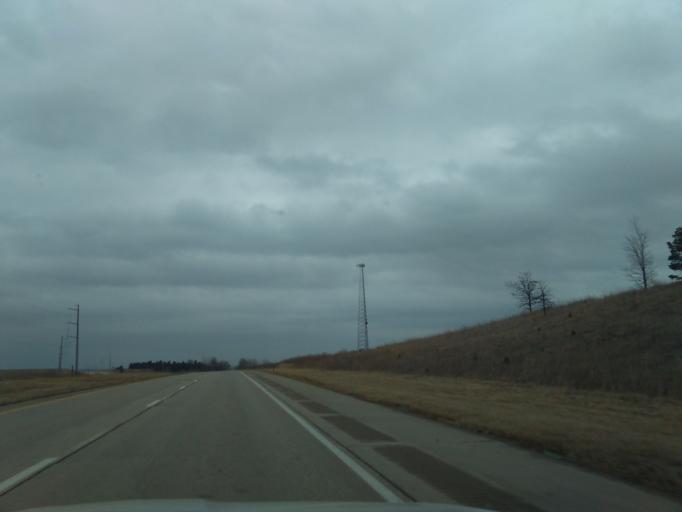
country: US
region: Nebraska
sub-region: Otoe County
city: Syracuse
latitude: 40.6683
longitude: -96.1171
